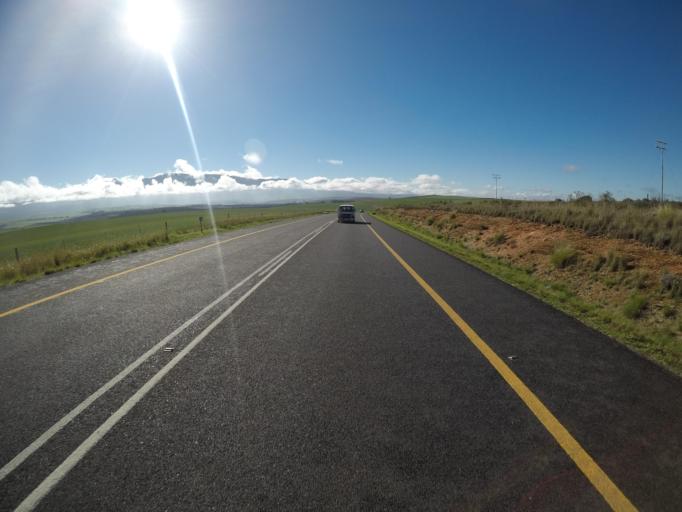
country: ZA
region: Western Cape
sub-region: Overberg District Municipality
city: Swellendam
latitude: -34.0875
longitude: 20.3920
